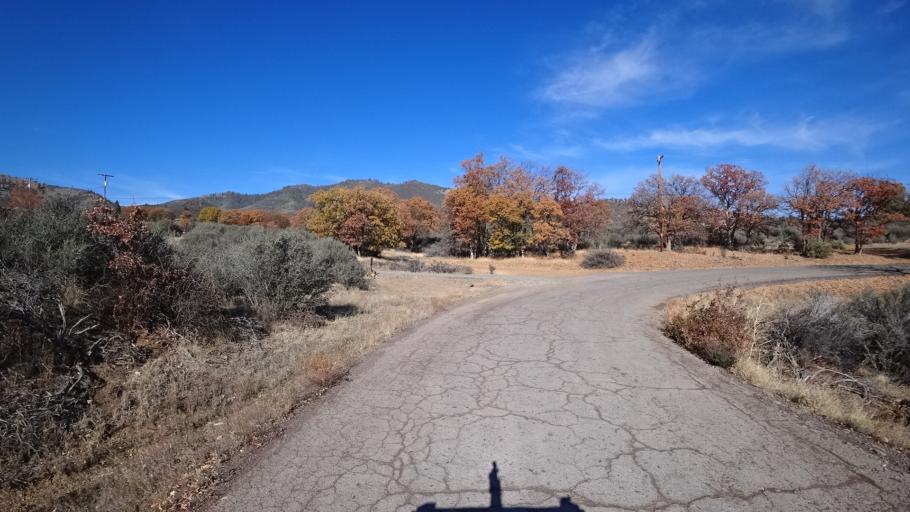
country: US
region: California
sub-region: Siskiyou County
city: Yreka
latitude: 41.7700
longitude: -122.6376
